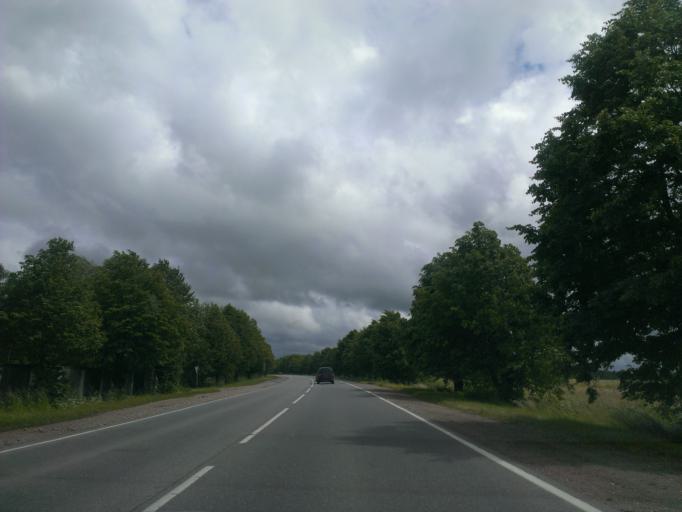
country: LV
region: Grobina
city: Grobina
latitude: 56.5332
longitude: 21.1091
